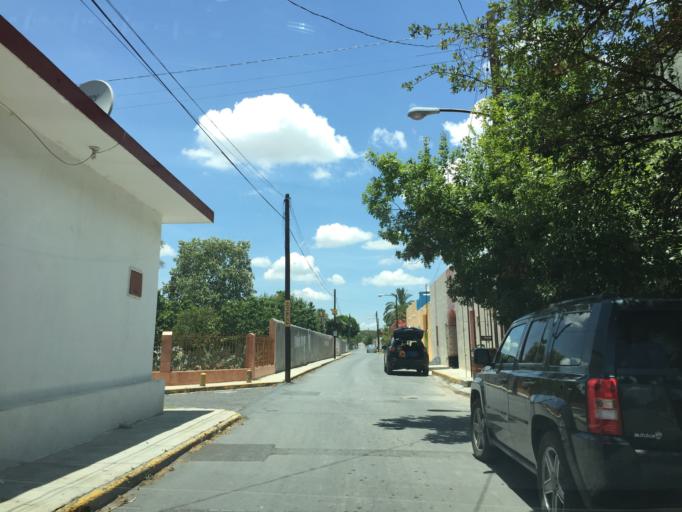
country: MX
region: Nuevo Leon
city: Marin
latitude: 25.8606
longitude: -99.9440
